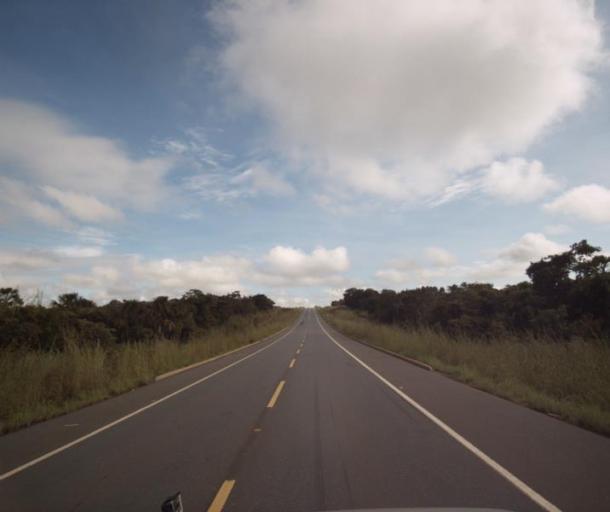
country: BR
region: Goias
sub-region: Barro Alto
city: Barro Alto
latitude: -15.2343
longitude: -48.6930
